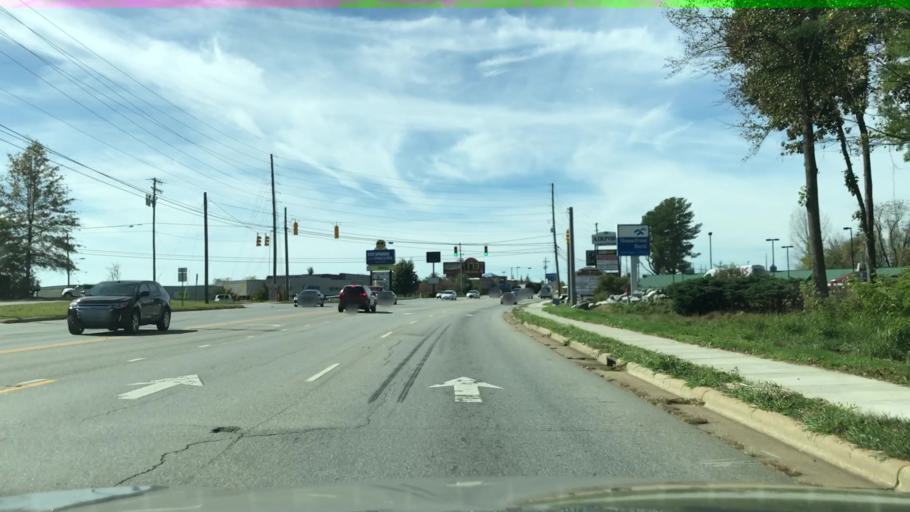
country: US
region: North Carolina
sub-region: Buncombe County
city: Royal Pines
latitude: 35.4530
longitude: -82.5234
